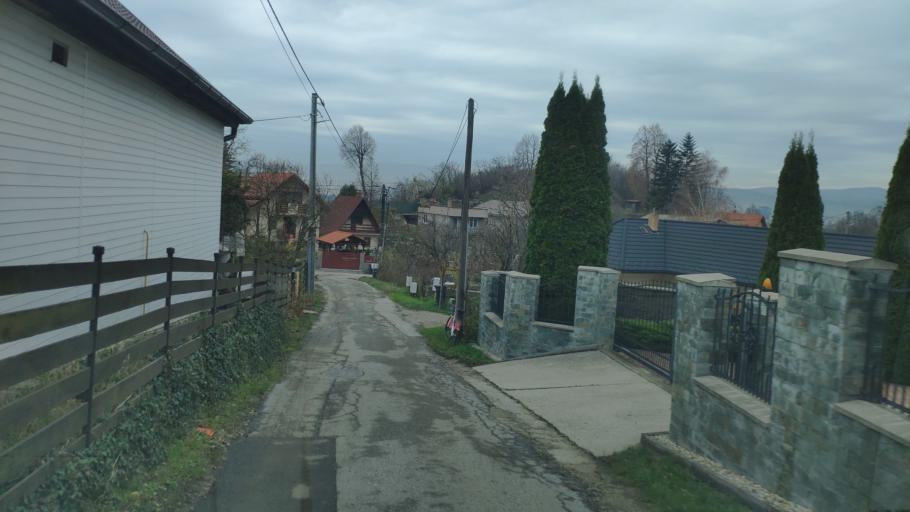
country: SK
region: Kosicky
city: Kosice
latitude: 48.7005
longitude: 21.2874
